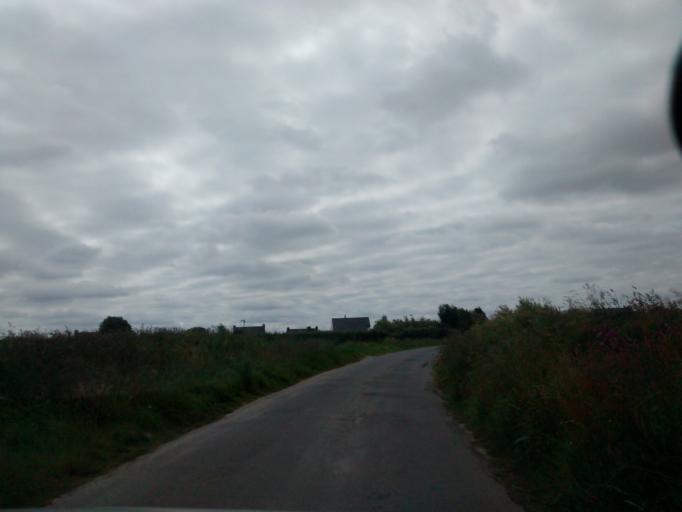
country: FR
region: Brittany
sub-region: Departement des Cotes-d'Armor
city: Penvenan
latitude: 48.8100
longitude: -3.3035
